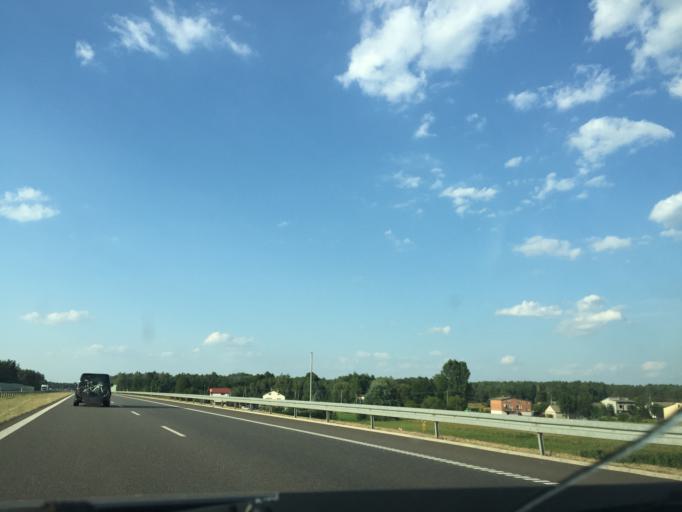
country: PL
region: Masovian Voivodeship
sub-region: Powiat radomski
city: Zakrzew
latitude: 51.4300
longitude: 21.0327
